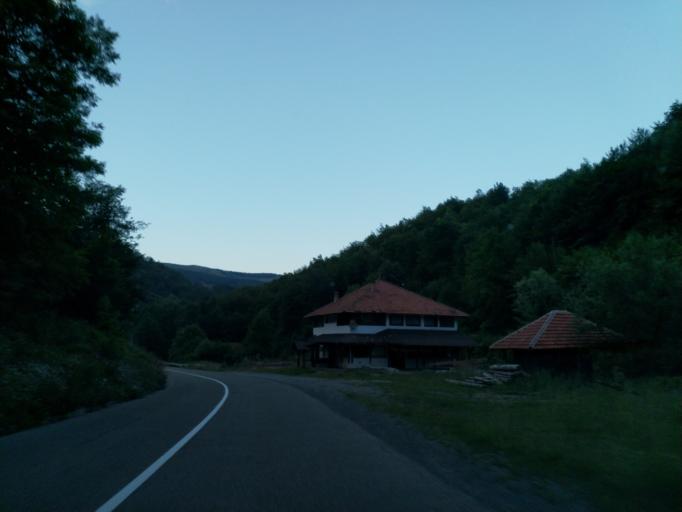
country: RS
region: Central Serbia
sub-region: Rasinski Okrug
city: Aleksandrovac
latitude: 43.3331
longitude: 20.9270
